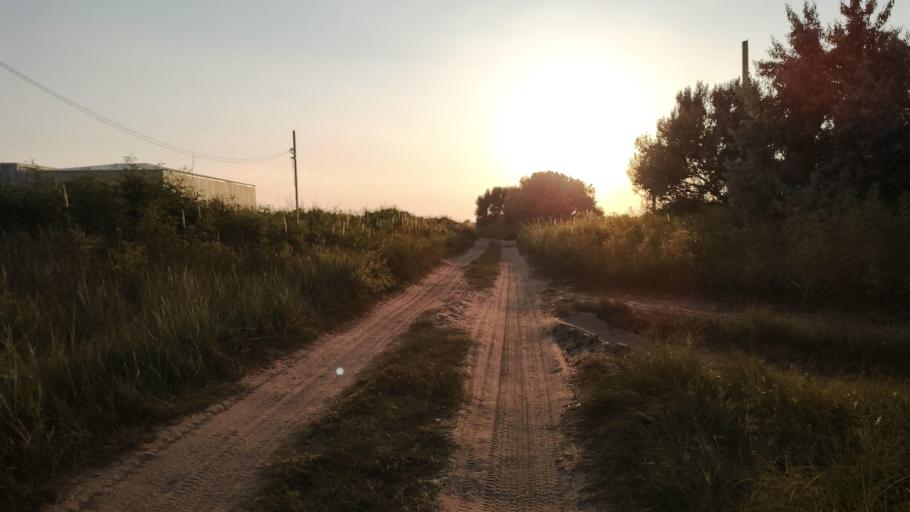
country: RU
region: Krasnodarskiy
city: Blagovetschenskaya
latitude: 45.0675
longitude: 37.0359
